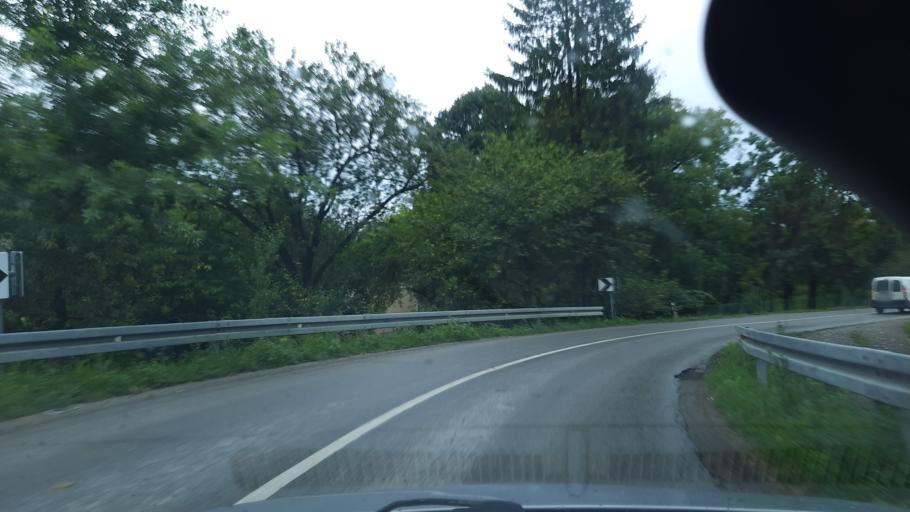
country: RS
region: Central Serbia
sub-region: Raski Okrug
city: Vrnjacka Banja
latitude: 43.7149
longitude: 20.8294
